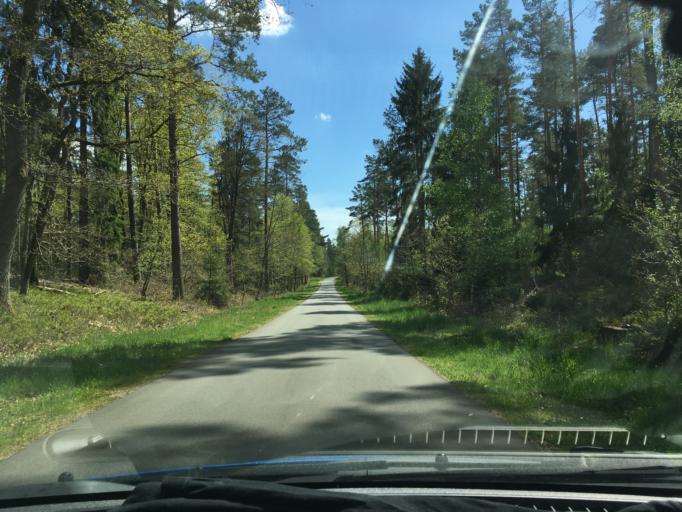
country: DE
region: Lower Saxony
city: Stoetze
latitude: 53.1010
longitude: 10.7820
